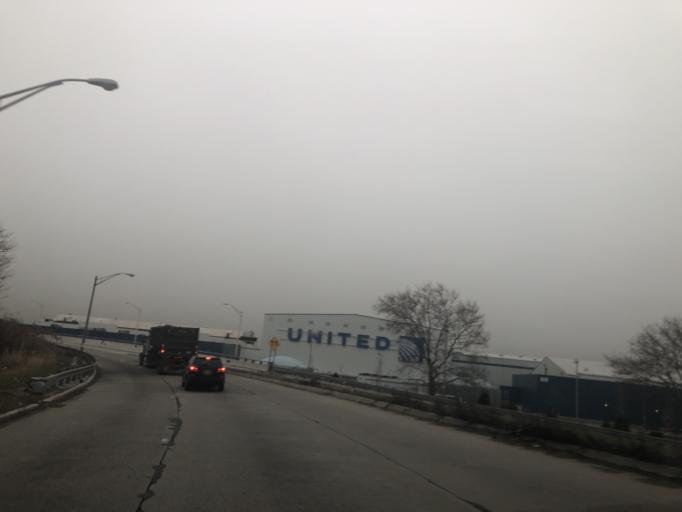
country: US
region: New Jersey
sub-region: Essex County
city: Newark
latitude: 40.7095
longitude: -74.1667
